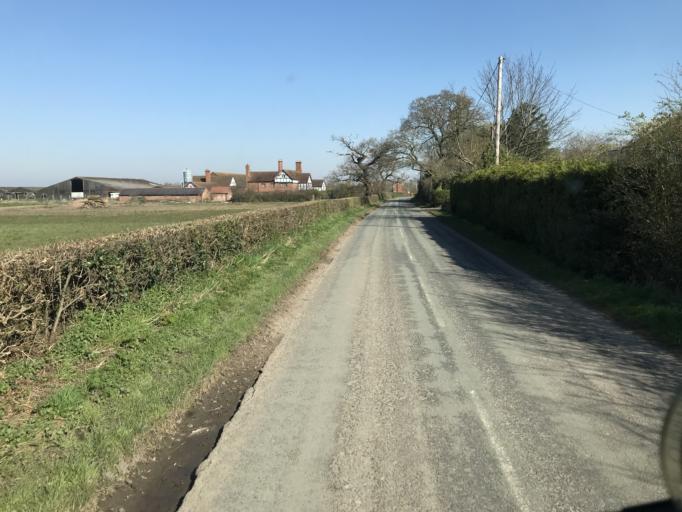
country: GB
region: England
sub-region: Cheshire West and Chester
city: Waverton
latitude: 53.1599
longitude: -2.8285
